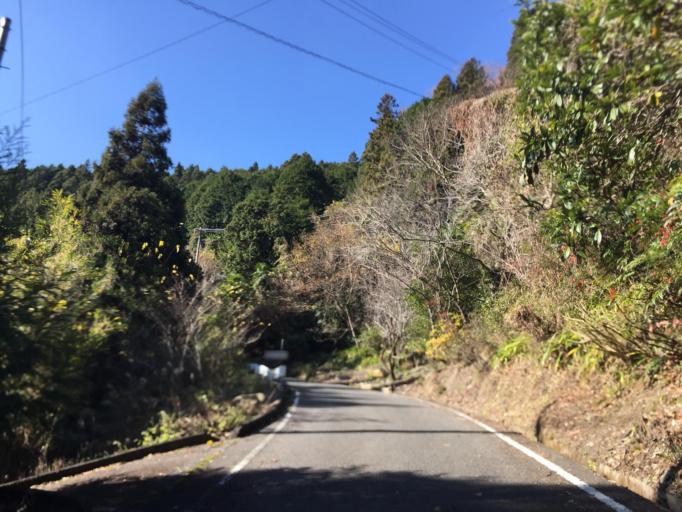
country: JP
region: Wakayama
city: Iwade
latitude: 34.1448
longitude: 135.4147
